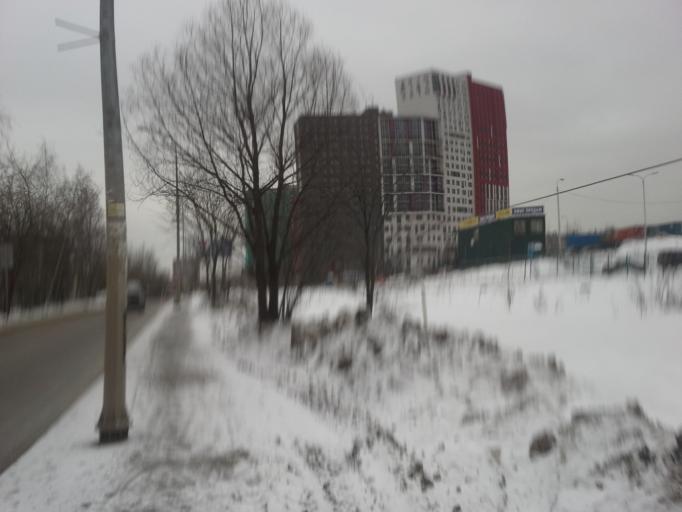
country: RU
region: Moskovskaya
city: Kommunarka
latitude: 55.5750
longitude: 37.4843
